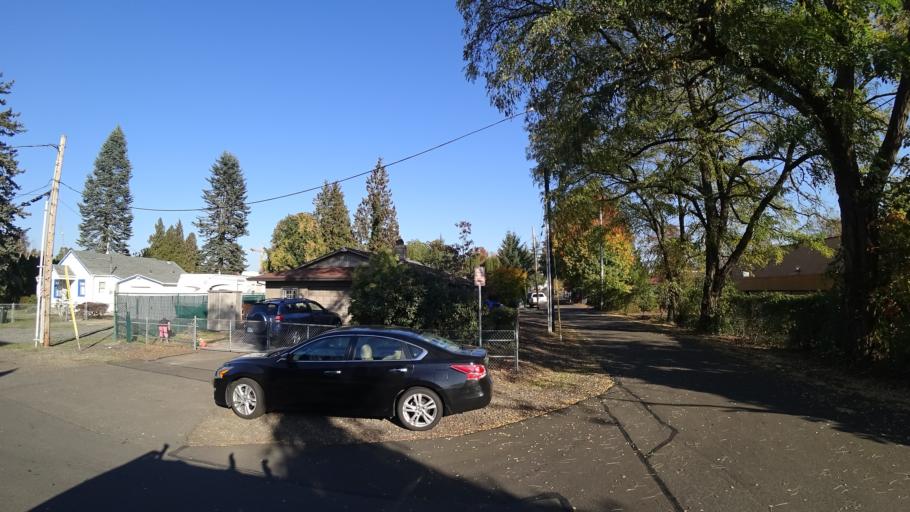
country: US
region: Oregon
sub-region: Multnomah County
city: Gresham
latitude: 45.5030
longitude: -122.4340
